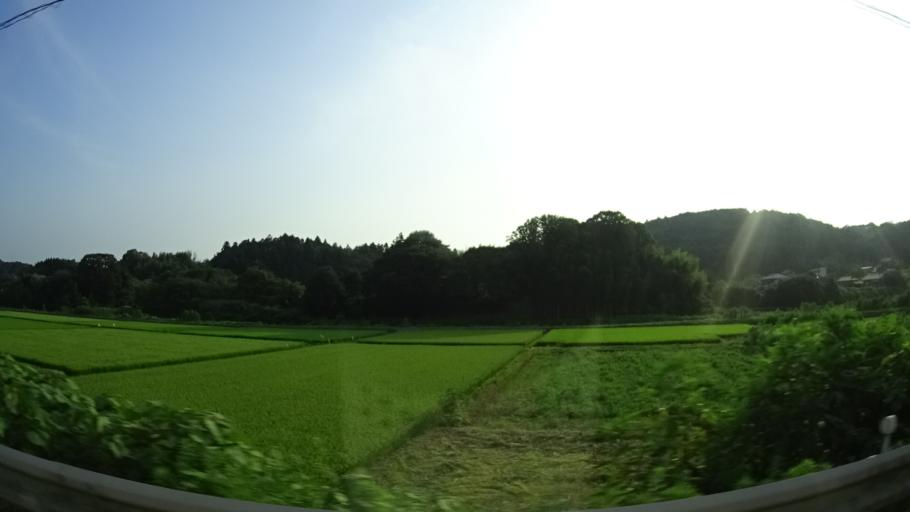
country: JP
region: Tochigi
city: Karasuyama
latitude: 36.6284
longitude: 140.1531
